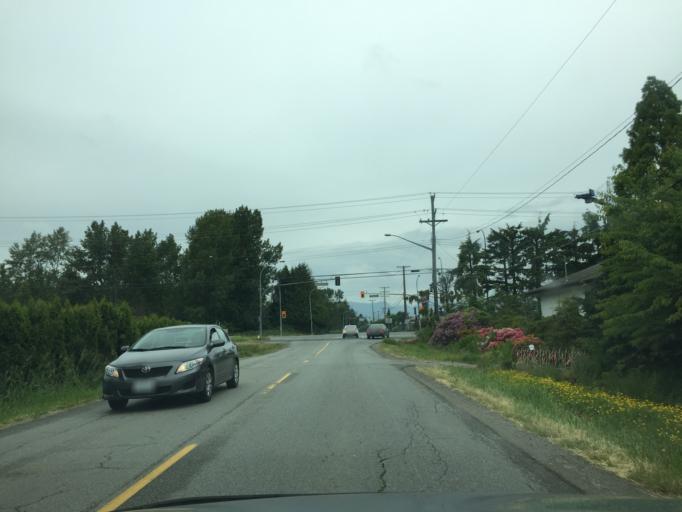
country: CA
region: British Columbia
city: Richmond
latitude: 49.1693
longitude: -123.0804
